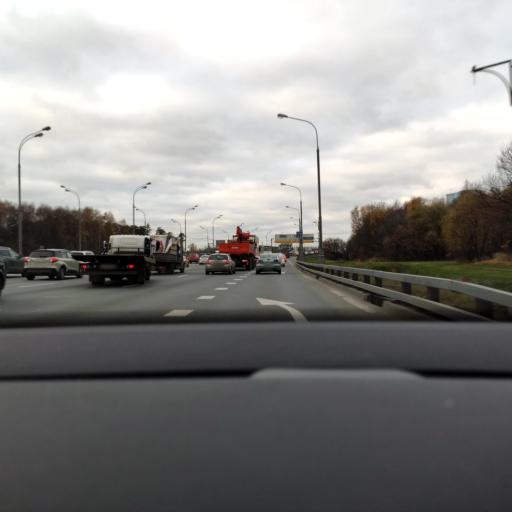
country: RU
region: Moskovskaya
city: Levoberezhnaya
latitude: 55.8838
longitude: 37.4644
